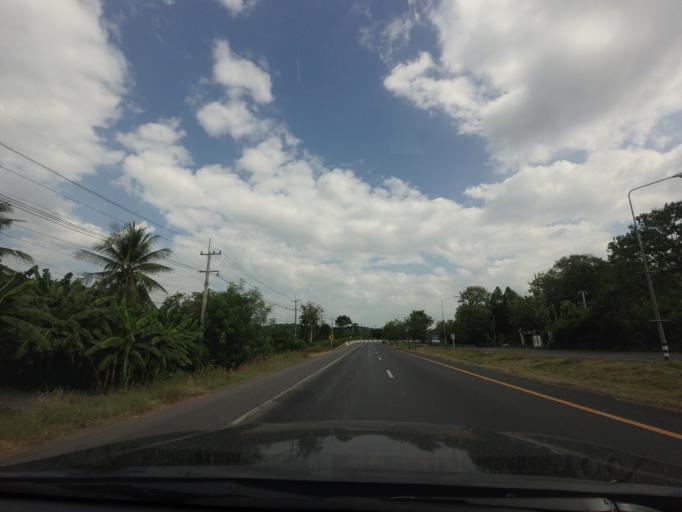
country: TH
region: Lop Buri
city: Chai Badan
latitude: 15.3001
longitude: 101.1276
